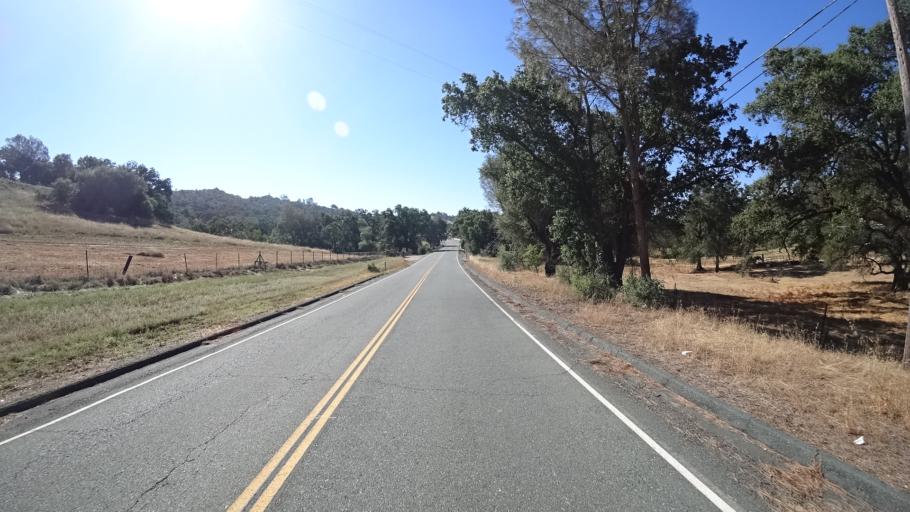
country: US
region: California
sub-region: Calaveras County
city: San Andreas
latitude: 38.2270
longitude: -120.7011
